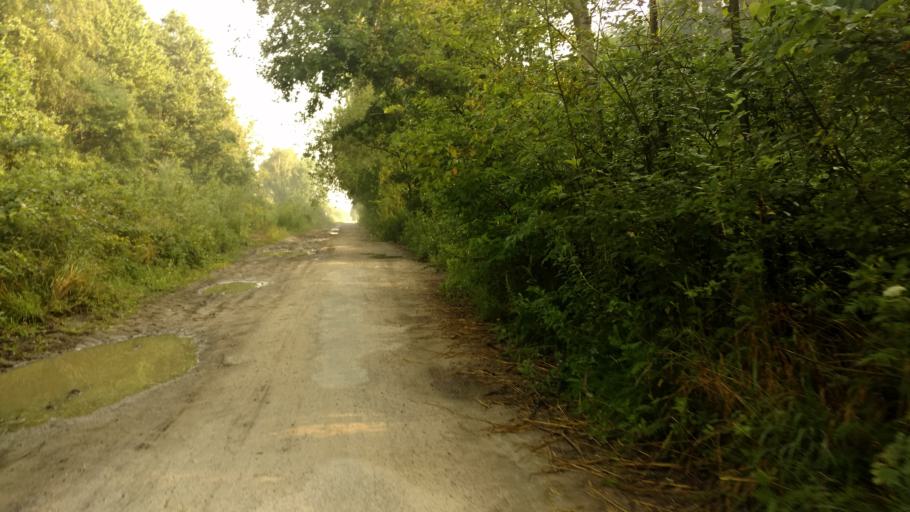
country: PL
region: Silesian Voivodeship
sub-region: Powiat pszczynski
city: Jankowice
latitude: 50.0112
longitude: 18.9743
